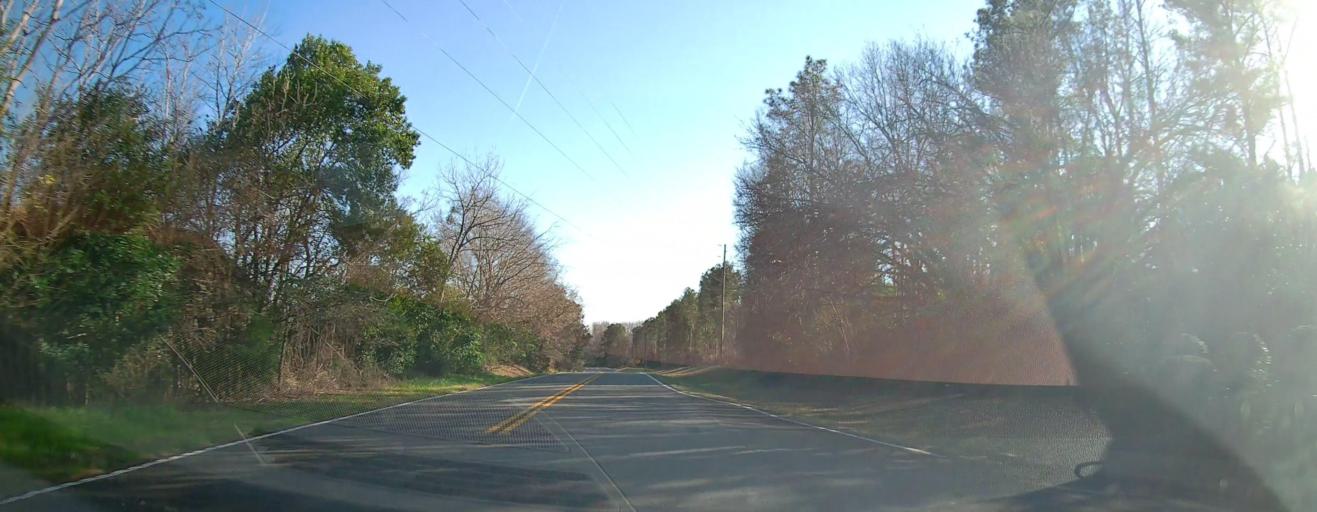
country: US
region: Georgia
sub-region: Sumter County
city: Americus
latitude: 32.0198
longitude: -84.2192
